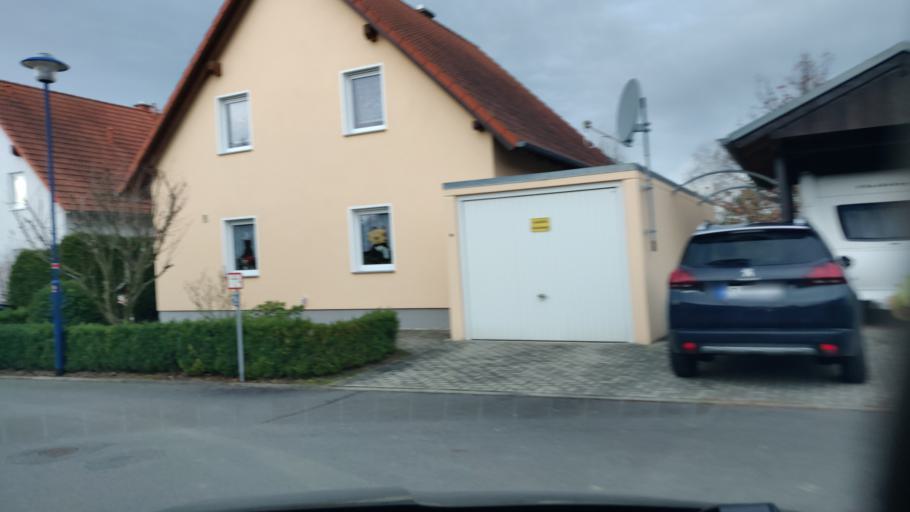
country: DE
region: Saxony
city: Bad Lausick
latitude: 51.1541
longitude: 12.6526
